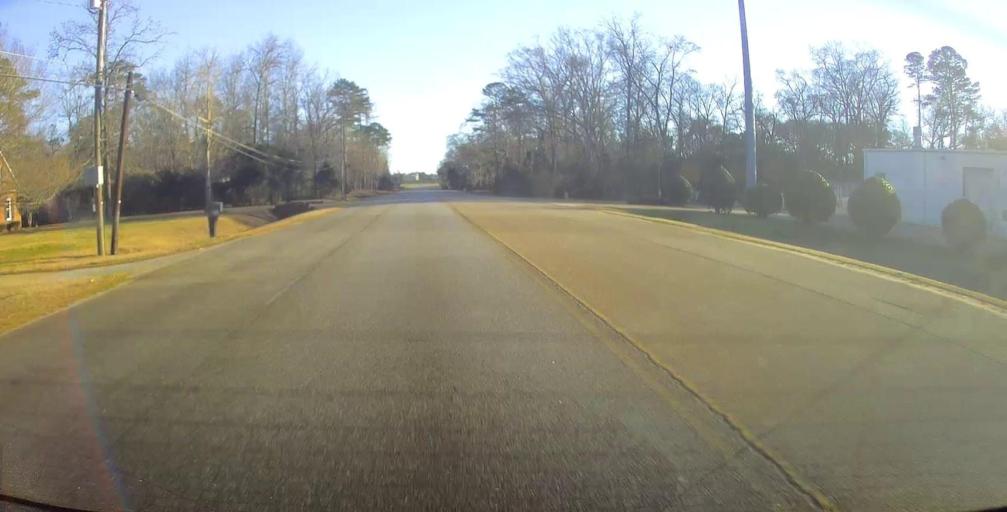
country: US
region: Georgia
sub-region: Dougherty County
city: Albany
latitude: 31.6278
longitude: -84.2295
